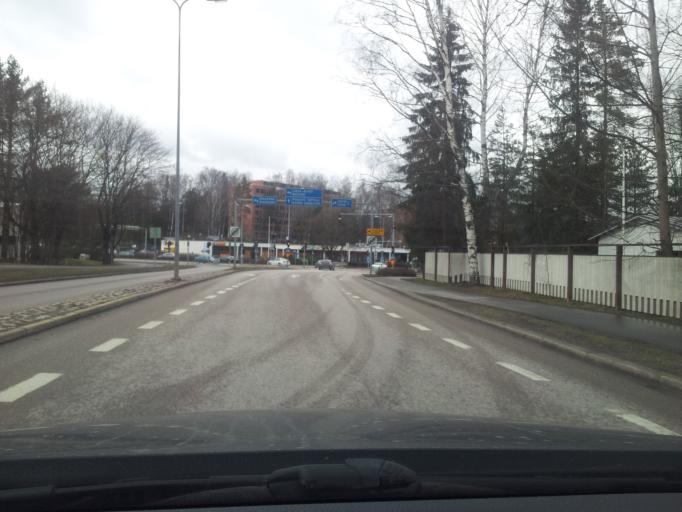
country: FI
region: Uusimaa
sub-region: Helsinki
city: Otaniemi
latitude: 60.1820
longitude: 24.7953
